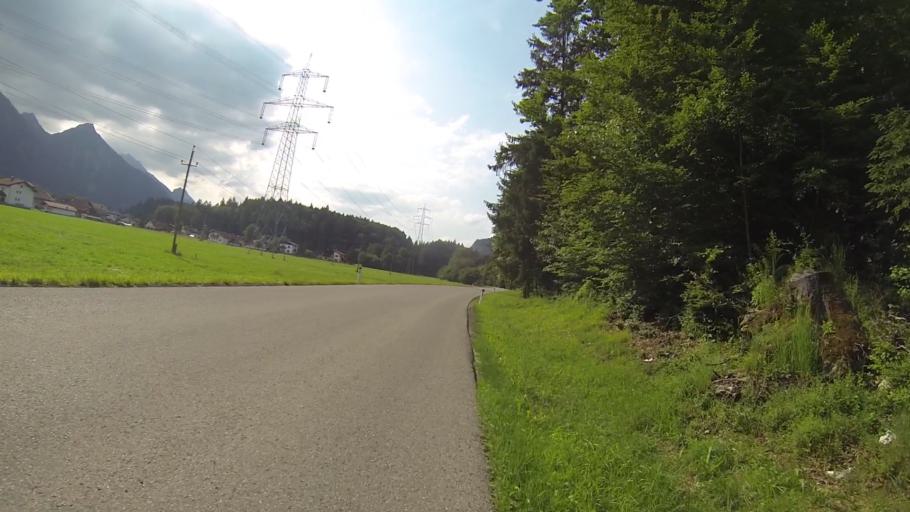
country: AT
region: Tyrol
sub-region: Politischer Bezirk Reutte
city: Musau
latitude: 47.5358
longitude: 10.6928
